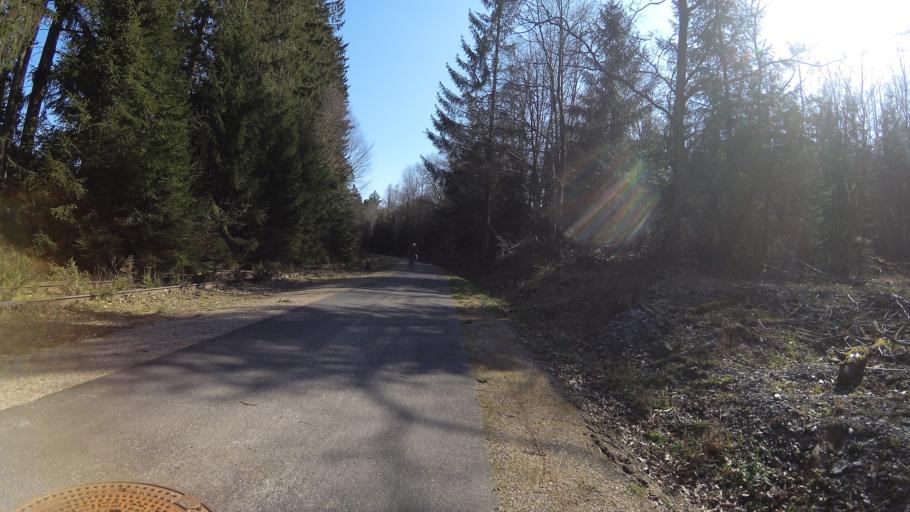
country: DE
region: Rheinland-Pfalz
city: Hermeskeil
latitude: 49.6730
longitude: 6.9210
